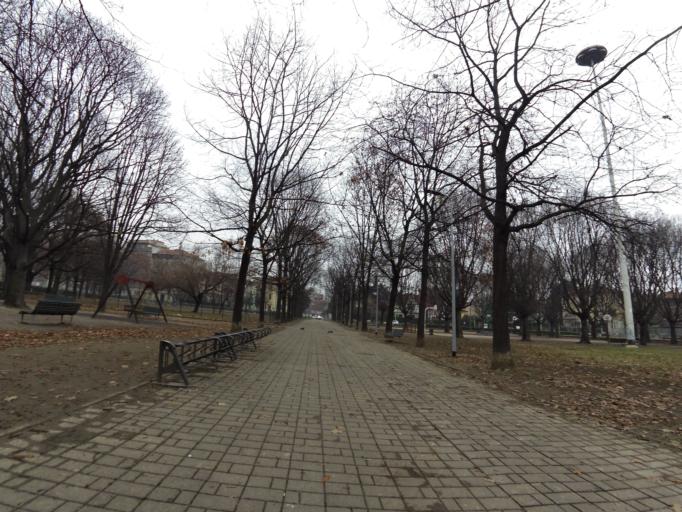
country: IT
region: Lombardy
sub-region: Citta metropolitana di Milano
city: Milano
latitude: 45.4468
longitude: 9.1836
